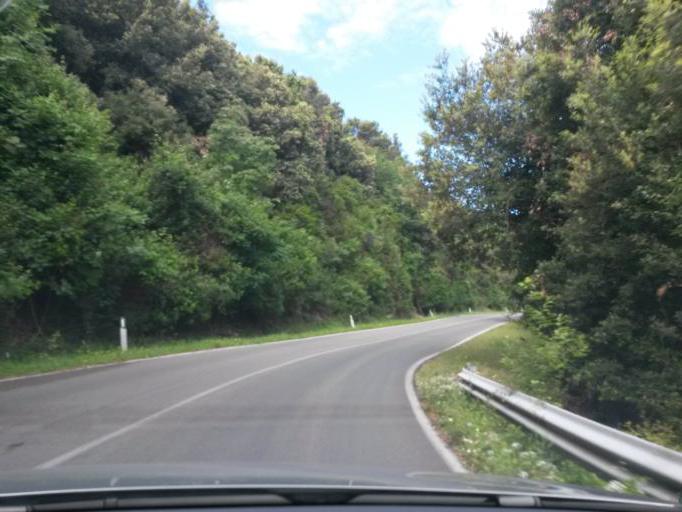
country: IT
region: Tuscany
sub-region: Provincia di Livorno
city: Marciana
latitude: 42.7972
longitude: 10.1695
